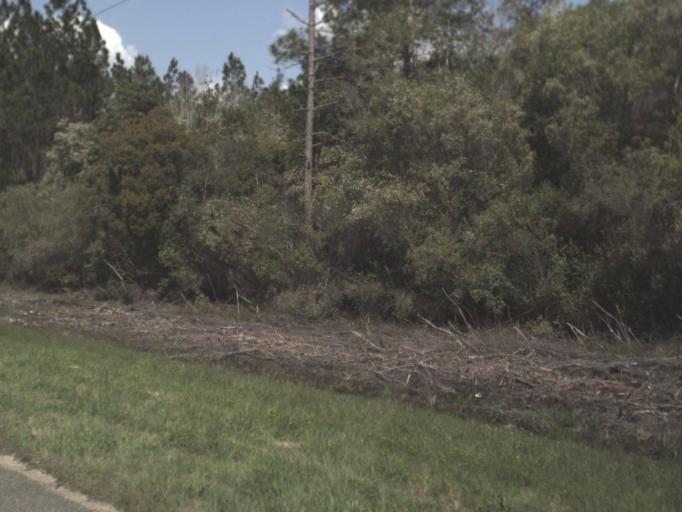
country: US
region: Florida
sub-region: Liberty County
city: Bristol
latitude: 30.4156
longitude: -84.8670
